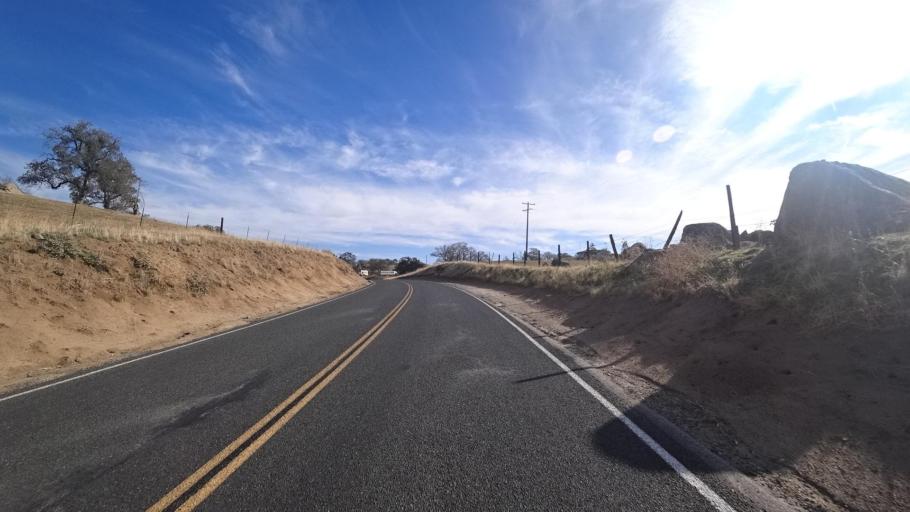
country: US
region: California
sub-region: Kern County
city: Oildale
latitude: 35.6179
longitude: -118.8517
